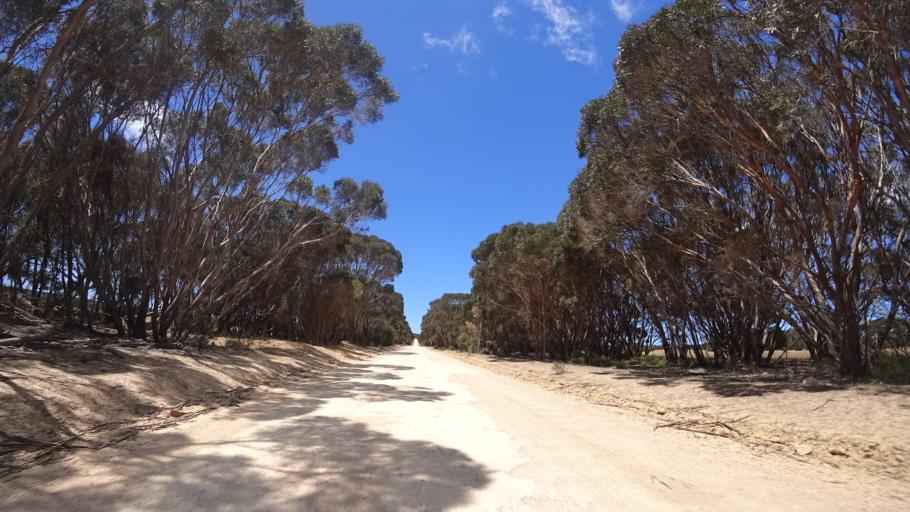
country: AU
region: South Australia
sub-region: Yankalilla
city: Normanville
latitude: -35.8239
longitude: 138.0805
